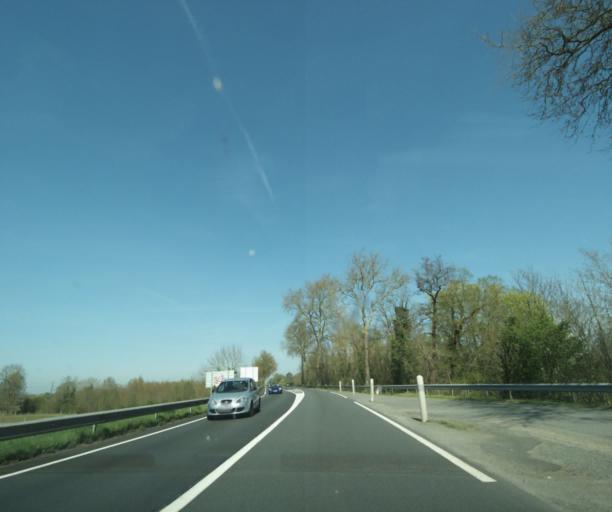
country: FR
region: Auvergne
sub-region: Departement de l'Allier
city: Trevol
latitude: 46.6263
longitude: 3.2855
